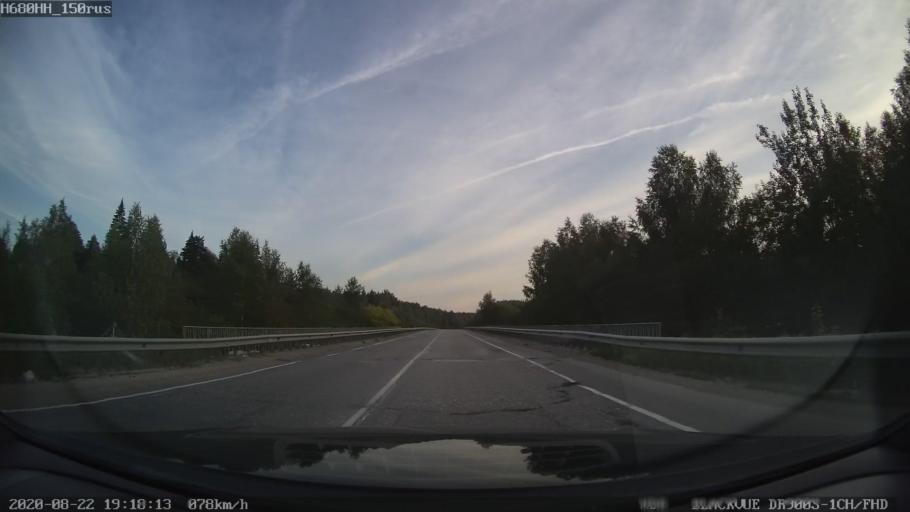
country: RU
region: Tverskaya
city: Sakharovo
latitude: 56.9374
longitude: 36.0068
